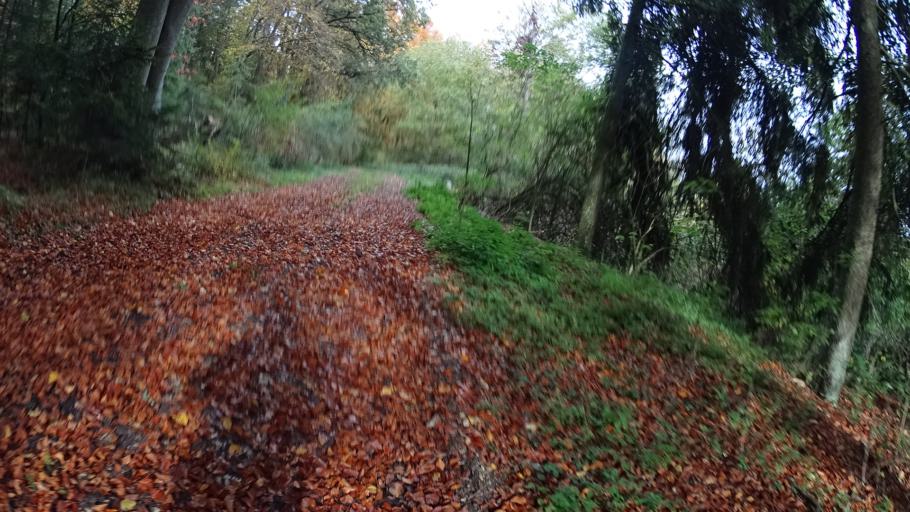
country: DE
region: Bavaria
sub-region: Upper Bavaria
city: Adelschlag
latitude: 48.8642
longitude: 11.2274
